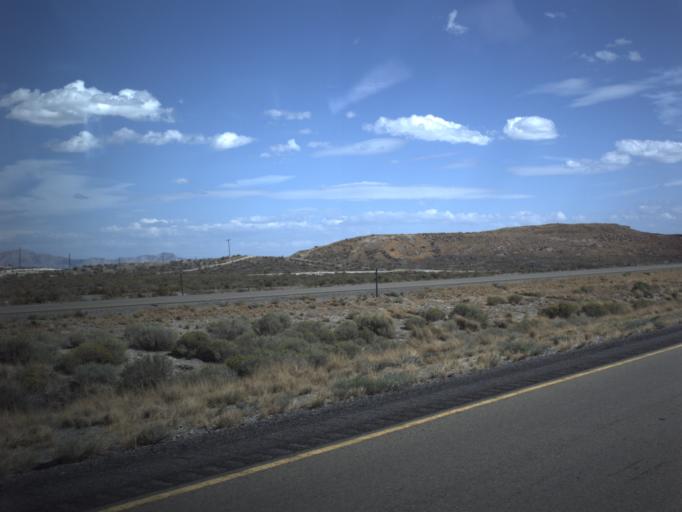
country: US
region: Utah
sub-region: Tooele County
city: Grantsville
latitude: 40.7643
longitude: -112.7845
